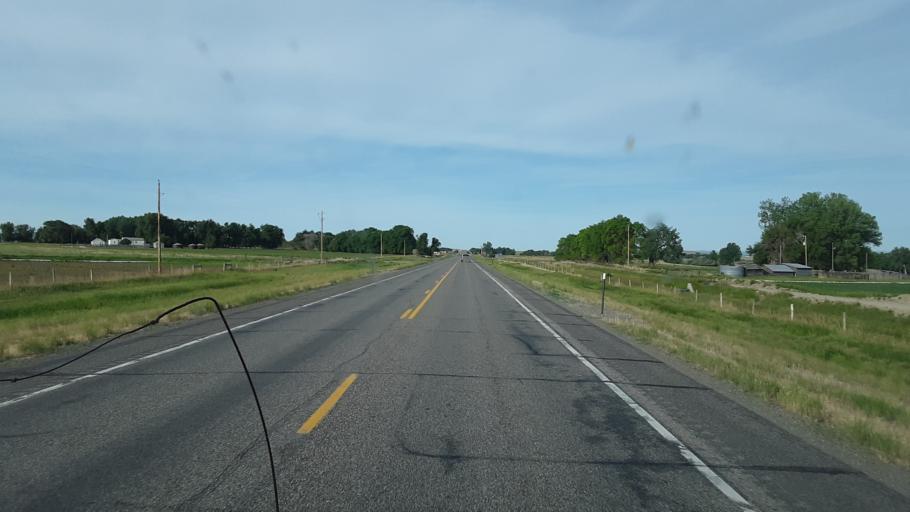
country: US
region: Wyoming
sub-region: Fremont County
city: Riverton
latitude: 43.1912
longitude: -108.2405
